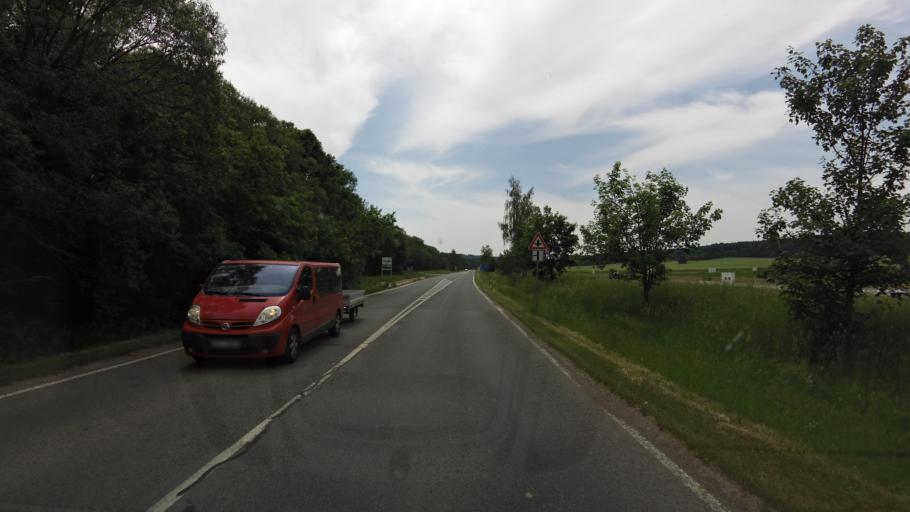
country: CZ
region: Plzensky
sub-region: Okres Rokycany
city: Rokycany
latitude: 49.7306
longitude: 13.5860
